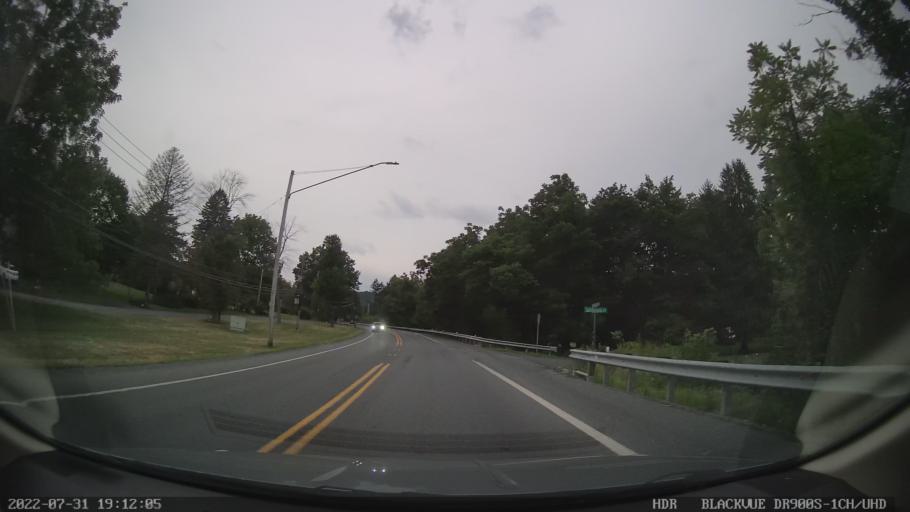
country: US
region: Pennsylvania
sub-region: Lehigh County
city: Fountain Hill
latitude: 40.5778
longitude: -75.3819
